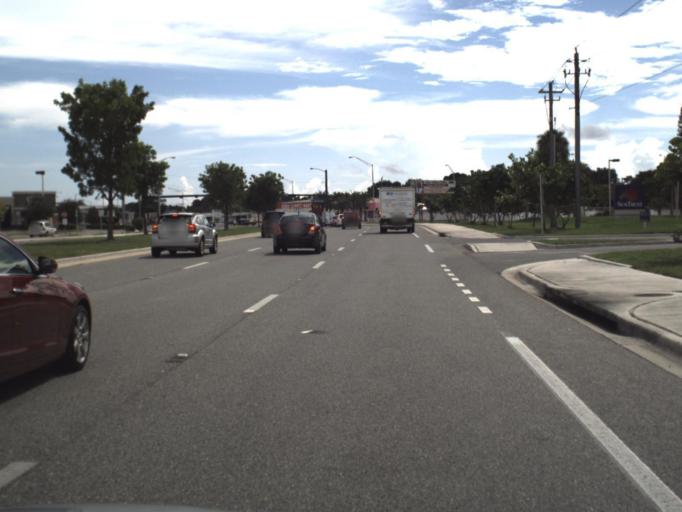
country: US
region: Florida
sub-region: Sarasota County
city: Venice Gardens
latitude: 27.0764
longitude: -82.4252
